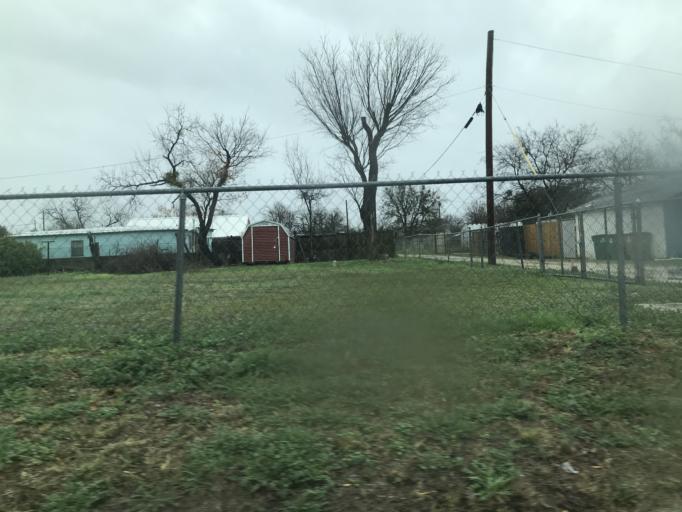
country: US
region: Texas
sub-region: Tom Green County
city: San Angelo
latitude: 31.4648
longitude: -100.4189
